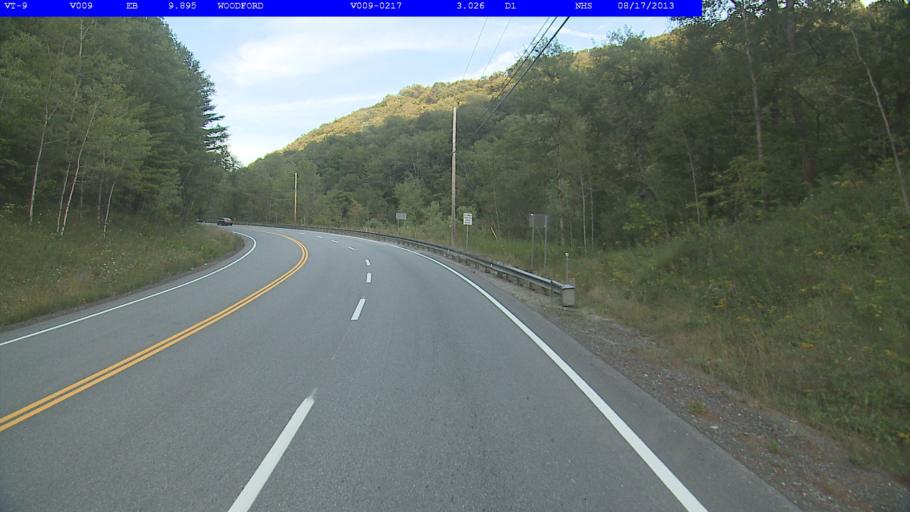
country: US
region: Vermont
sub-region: Bennington County
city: Bennington
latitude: 42.8781
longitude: -73.1157
